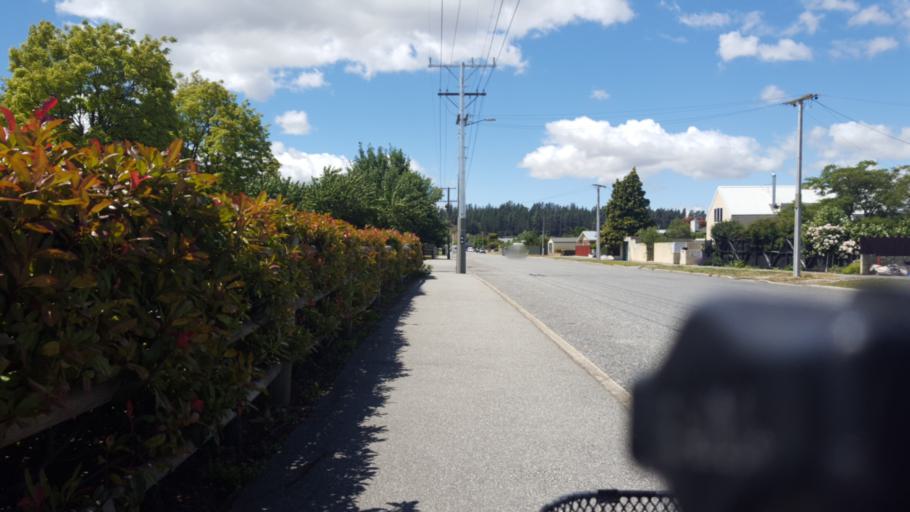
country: NZ
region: Otago
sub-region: Queenstown-Lakes District
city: Wanaka
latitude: -45.2465
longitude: 169.3865
